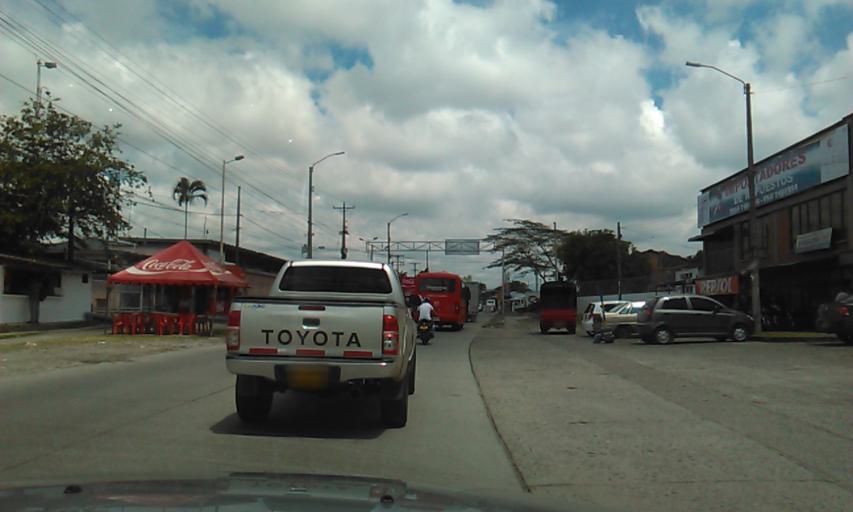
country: CO
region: Quindio
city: Armenia
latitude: 4.5094
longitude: -75.6902
